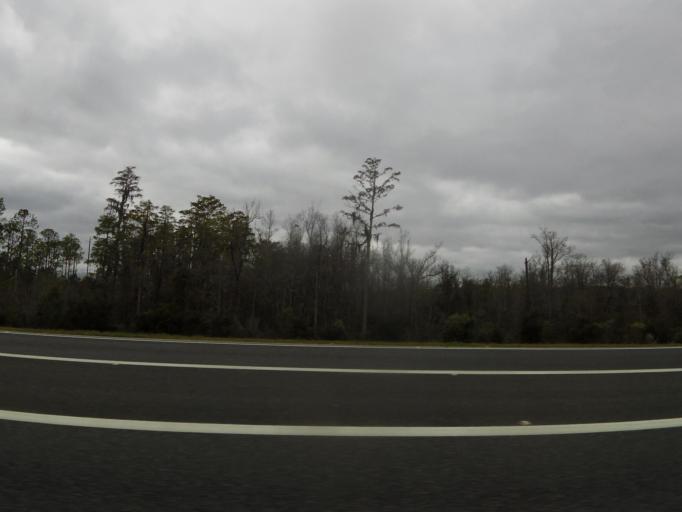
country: US
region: Florida
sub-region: Duval County
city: Baldwin
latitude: 30.2813
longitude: -81.8782
